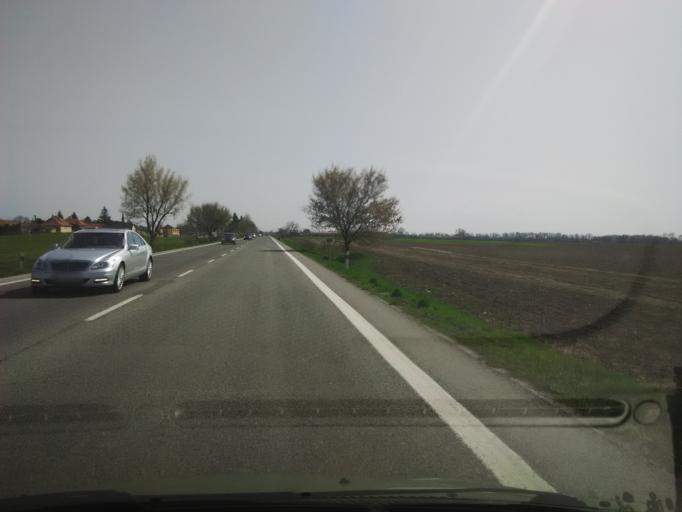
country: SK
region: Nitriansky
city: Sellye
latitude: 48.1692
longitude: 17.8336
